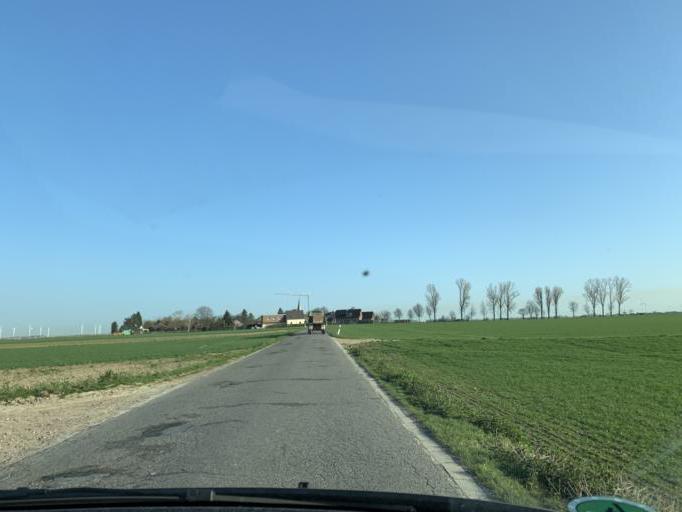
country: DE
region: North Rhine-Westphalia
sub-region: Regierungsbezirk Koln
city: Titz
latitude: 50.9838
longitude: 6.4623
